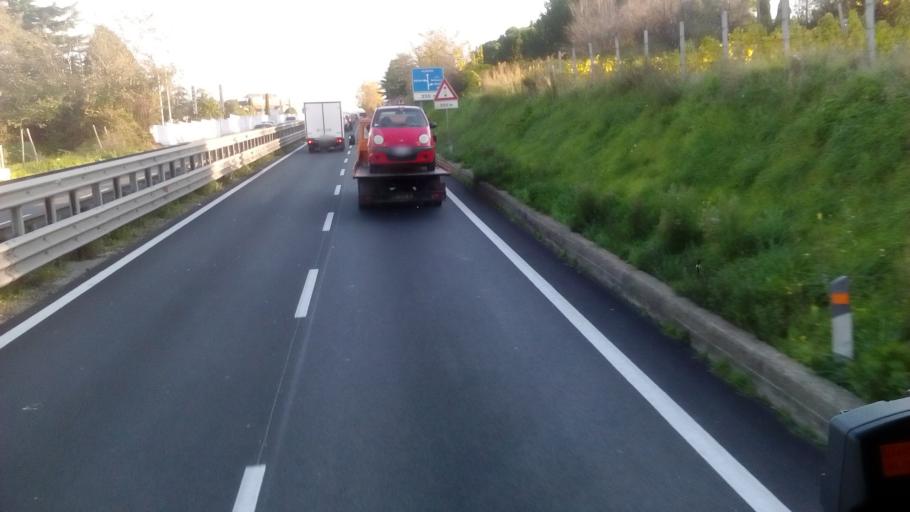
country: IT
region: Latium
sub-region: Citta metropolitana di Roma Capitale
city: Marino
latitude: 41.7698
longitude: 12.6137
